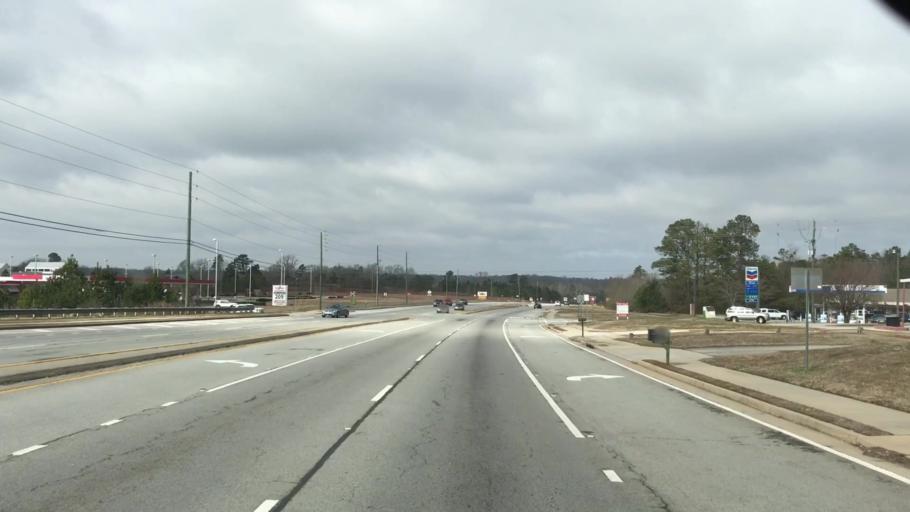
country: US
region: Georgia
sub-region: Hall County
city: Oakwood
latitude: 34.1877
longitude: -83.8553
